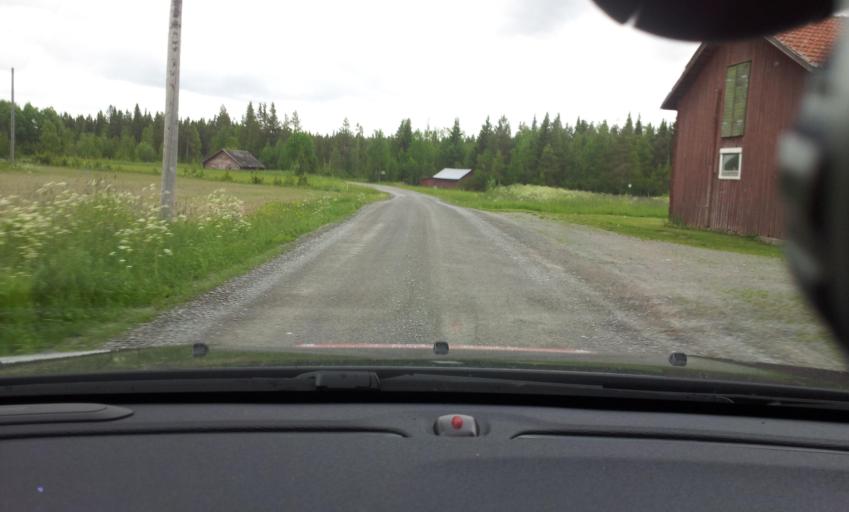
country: SE
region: Jaemtland
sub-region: OEstersunds Kommun
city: Brunflo
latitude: 63.1535
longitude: 15.0179
